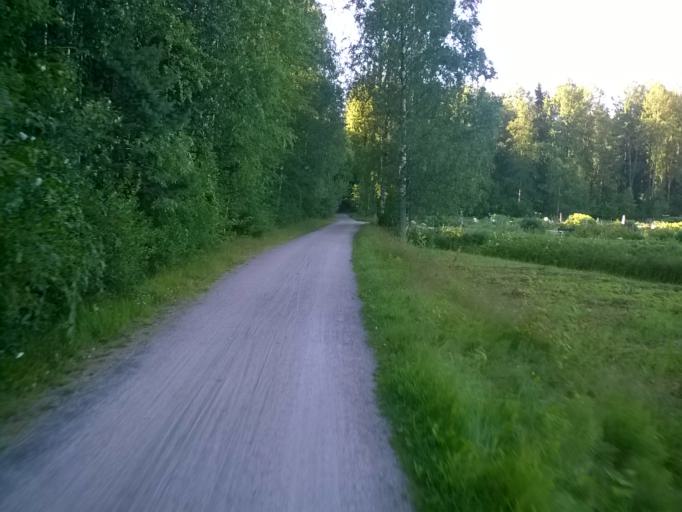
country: FI
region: Uusimaa
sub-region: Helsinki
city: Helsinki
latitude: 60.2260
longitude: 24.9135
